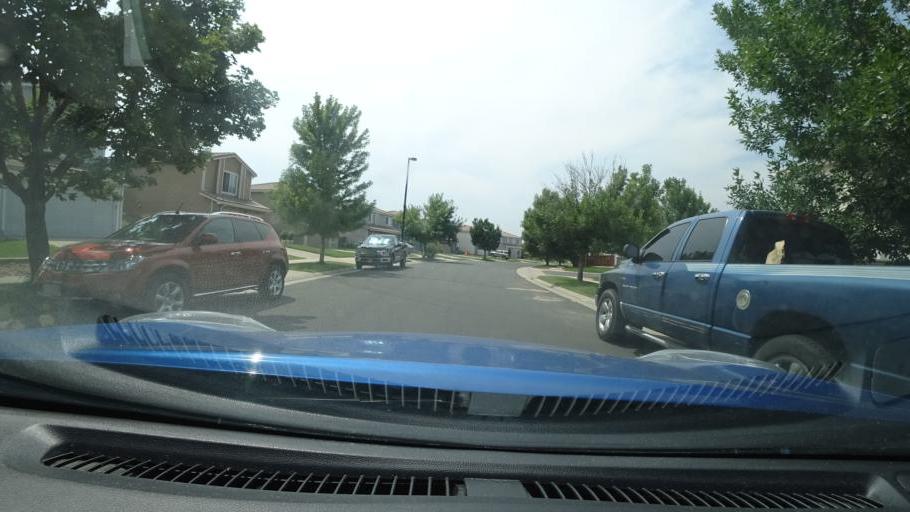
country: US
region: Colorado
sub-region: Adams County
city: Aurora
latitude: 39.7699
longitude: -104.7424
